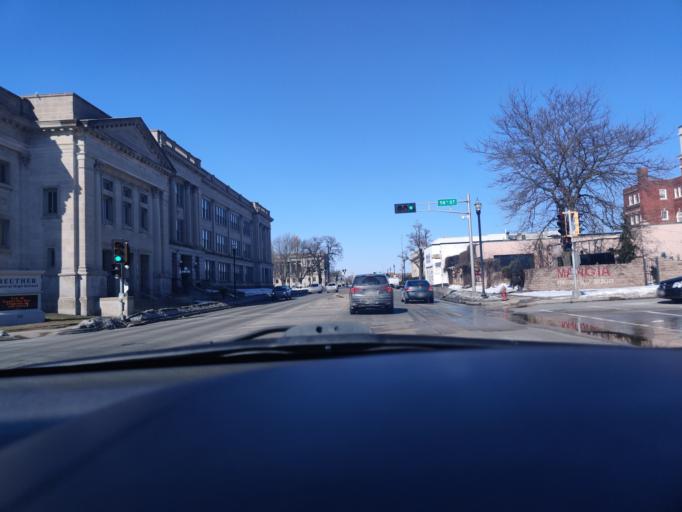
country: US
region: Wisconsin
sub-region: Kenosha County
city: Kenosha
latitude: 42.5827
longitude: -87.8218
